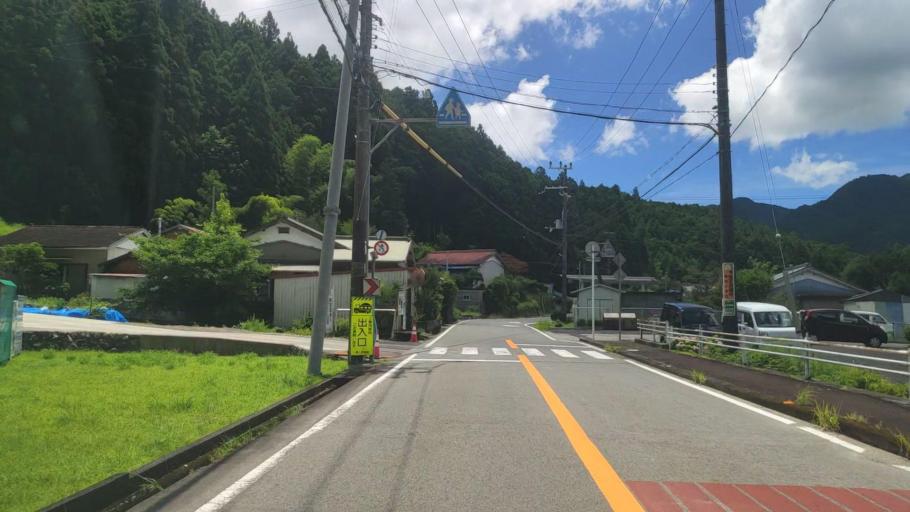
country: JP
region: Mie
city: Owase
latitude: 33.9482
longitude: 136.0768
